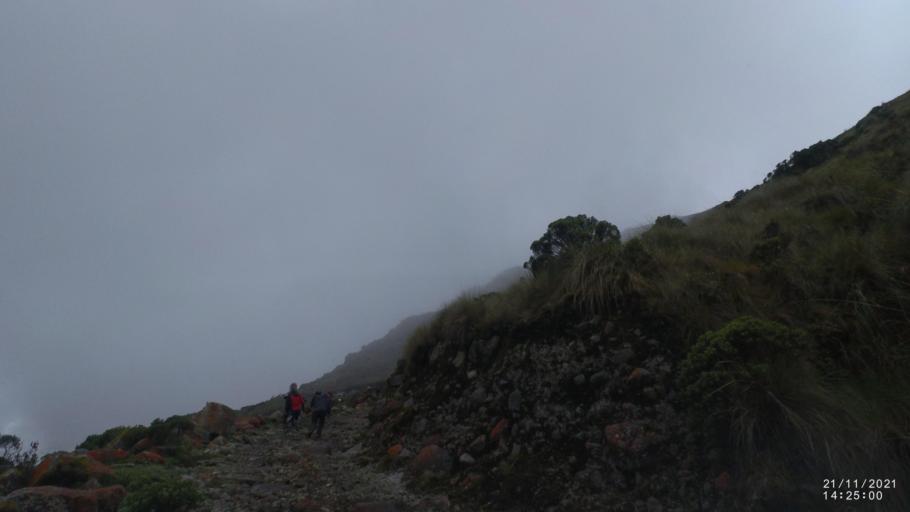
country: BO
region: Cochabamba
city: Cochabamba
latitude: -16.9456
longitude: -66.2579
